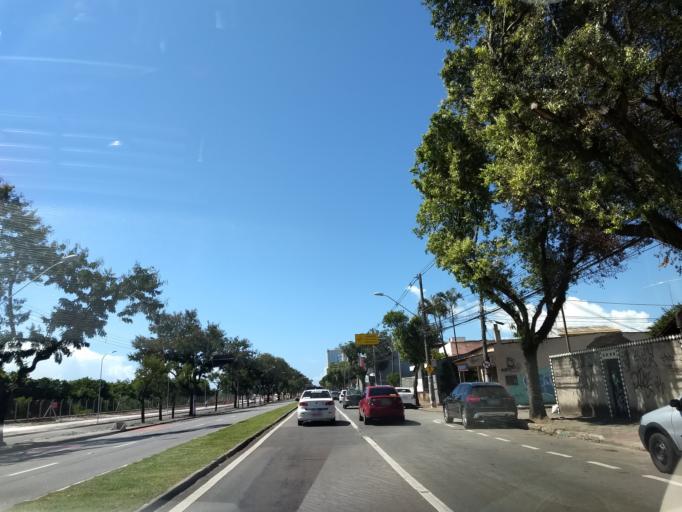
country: BR
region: Espirito Santo
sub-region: Vila Velha
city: Vila Velha
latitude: -20.2690
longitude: -40.2919
